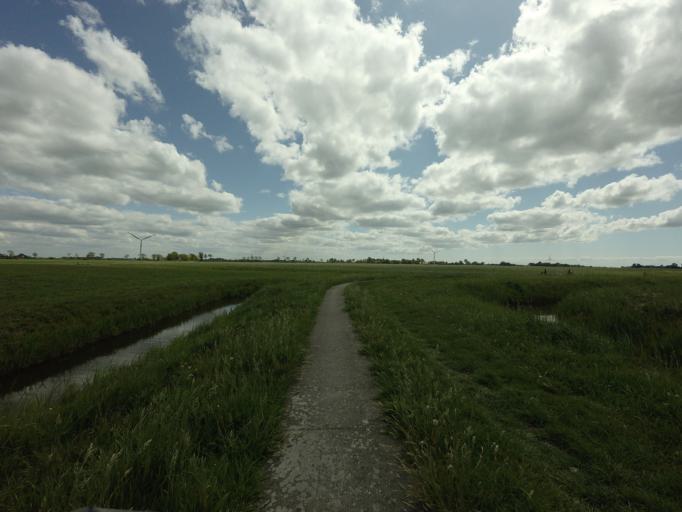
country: NL
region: Friesland
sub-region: Gemeente Littenseradiel
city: Wommels
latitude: 53.1308
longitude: 5.5725
